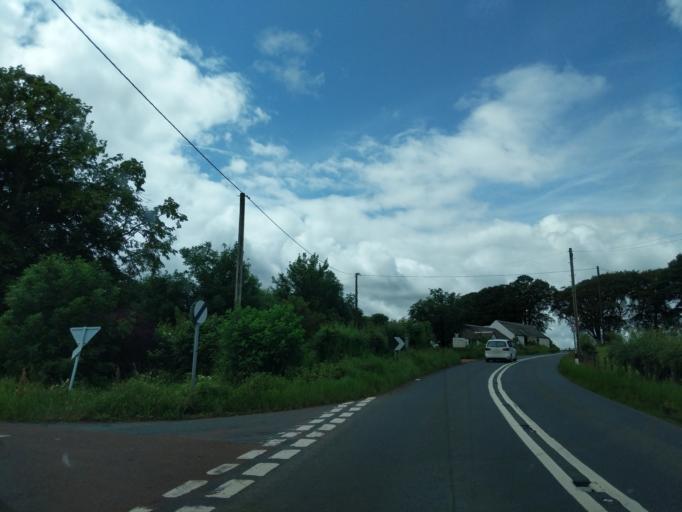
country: GB
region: Scotland
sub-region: South Lanarkshire
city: Biggar
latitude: 55.6049
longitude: -3.5823
